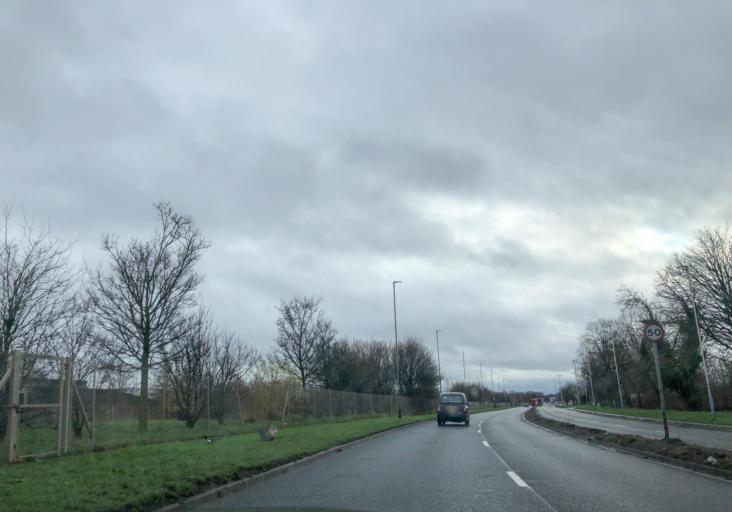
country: GB
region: England
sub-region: Buckinghamshire
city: Iver
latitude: 51.4699
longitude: -0.4917
